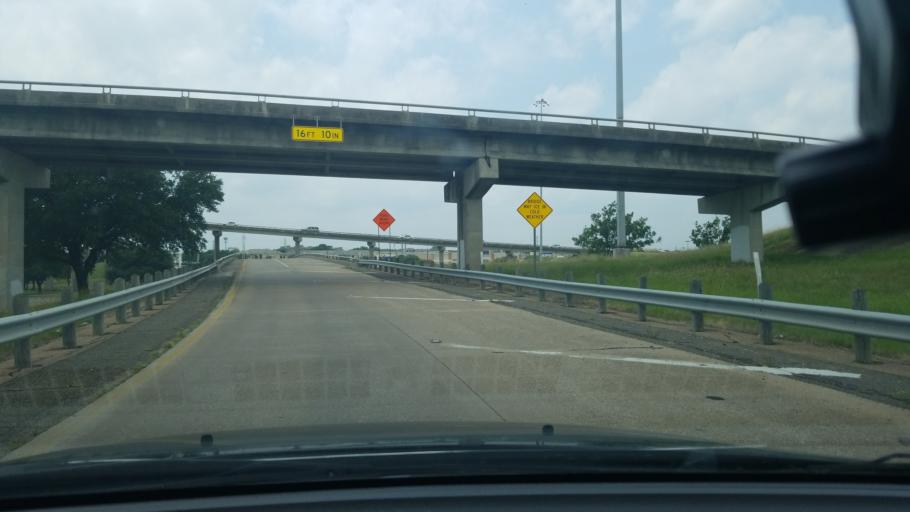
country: US
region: Texas
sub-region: Dallas County
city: Mesquite
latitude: 32.7940
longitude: -96.6240
